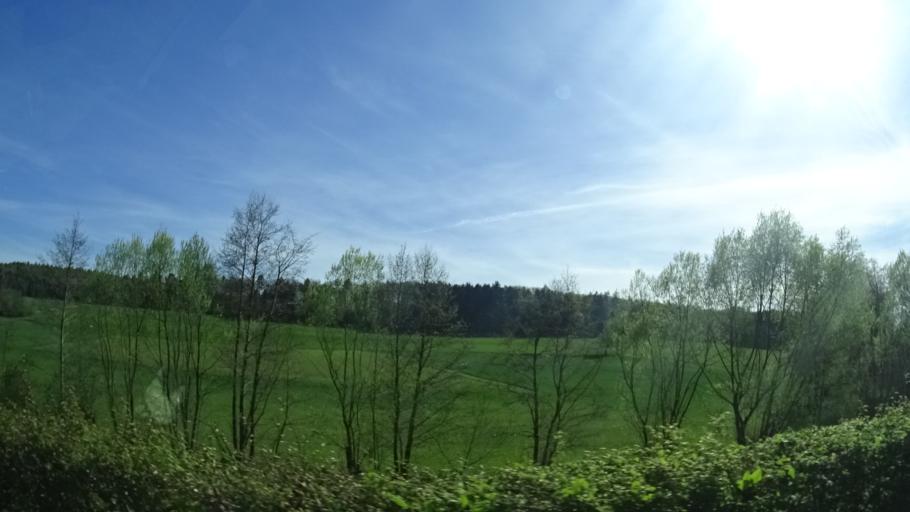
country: DE
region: Bavaria
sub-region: Regierungsbezirk Unterfranken
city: Burgpreppach
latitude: 50.1036
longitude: 10.6471
